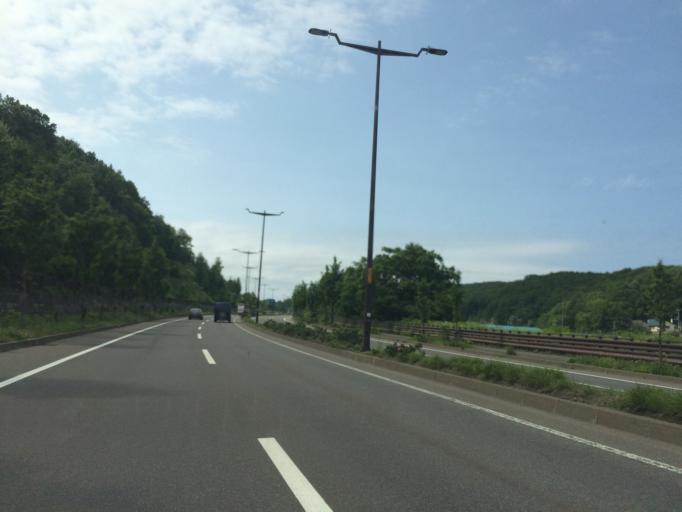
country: JP
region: Hokkaido
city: Otaru
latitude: 43.2138
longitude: 140.9589
